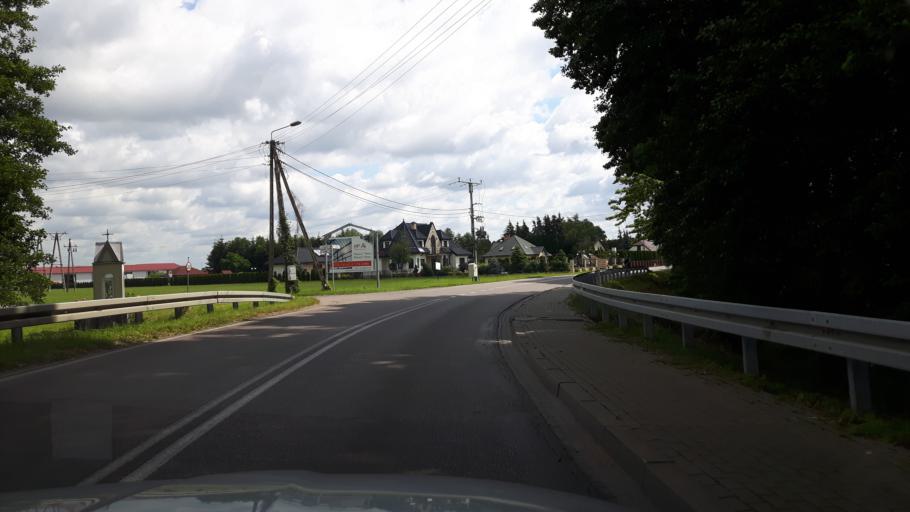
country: PL
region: Masovian Voivodeship
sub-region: Powiat ostrowski
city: Brok
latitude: 52.7046
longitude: 21.8852
